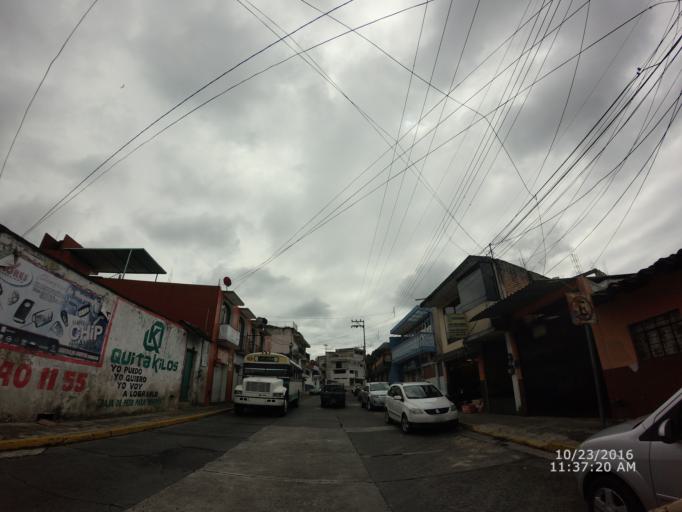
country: MX
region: Veracruz
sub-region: Xalapa
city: Xalapa de Enriquez
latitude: 19.5352
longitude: -96.9290
